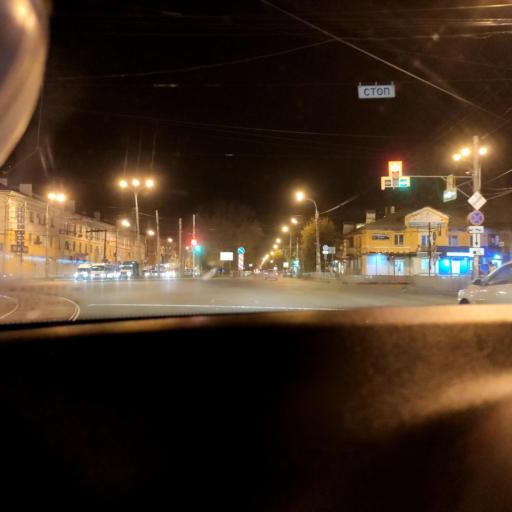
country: RU
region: Samara
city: Samara
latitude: 53.2197
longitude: 50.2632
